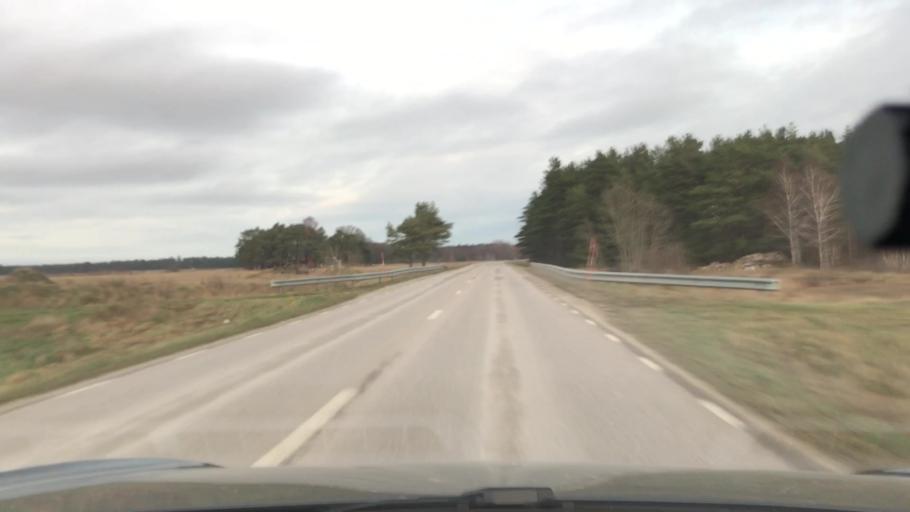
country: SE
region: Gotland
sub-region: Gotland
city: Slite
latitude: 57.7161
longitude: 18.5513
